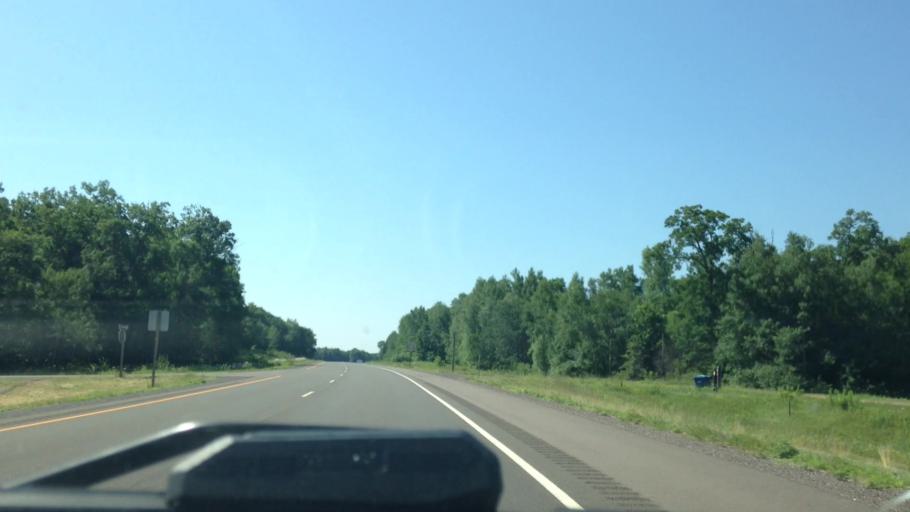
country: US
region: Wisconsin
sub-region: Washburn County
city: Spooner
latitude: 45.9430
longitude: -91.8292
